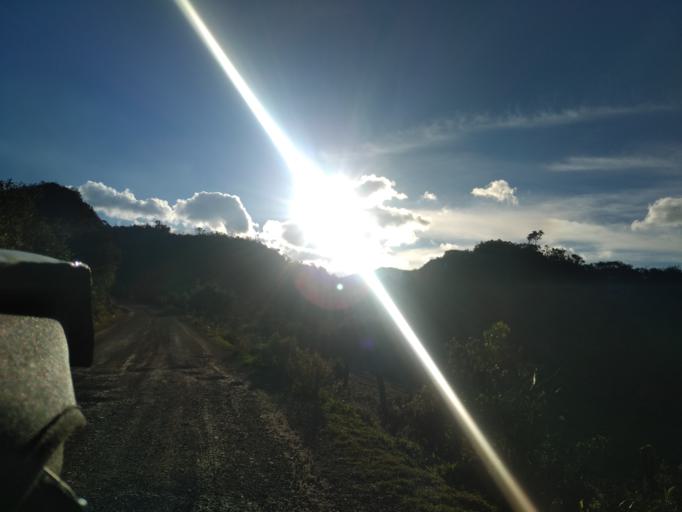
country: PE
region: Amazonas
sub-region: Provincia de Chachapoyas
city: Montevideo
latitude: -6.7103
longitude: -77.8665
